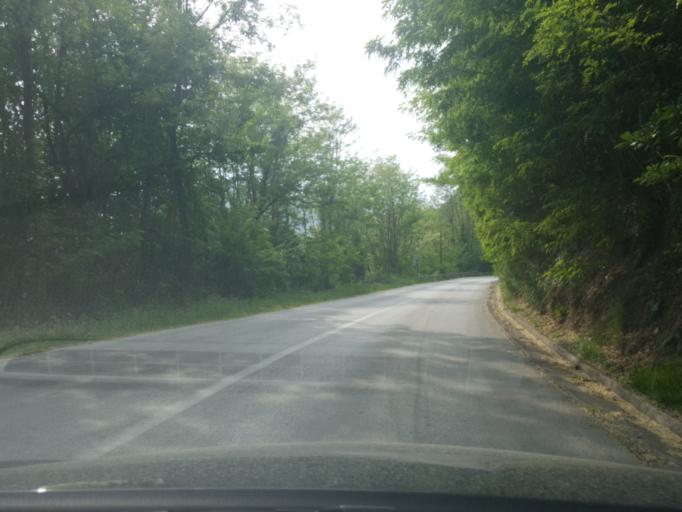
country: RS
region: Central Serbia
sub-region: Zlatiborski Okrug
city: Bajina Basta
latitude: 44.0416
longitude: 19.6263
